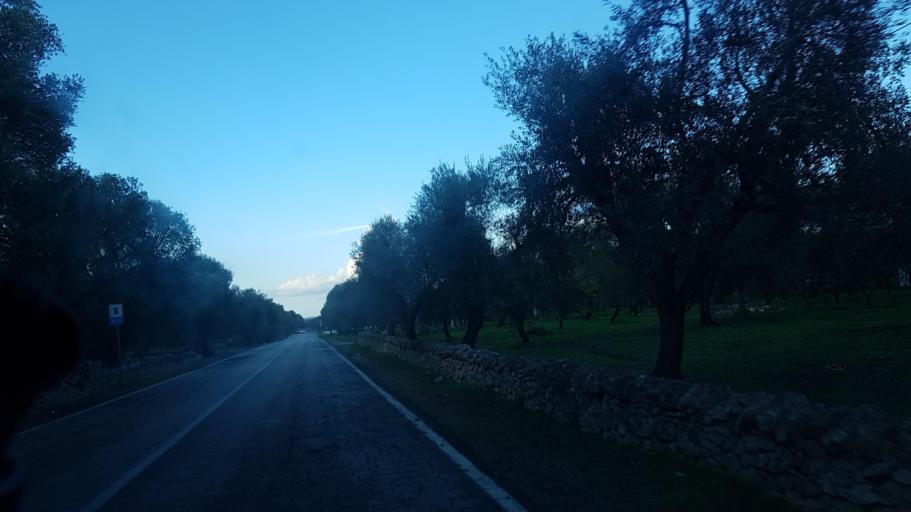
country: IT
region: Apulia
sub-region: Provincia di Brindisi
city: San Michele Salentino
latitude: 40.6486
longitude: 17.6067
